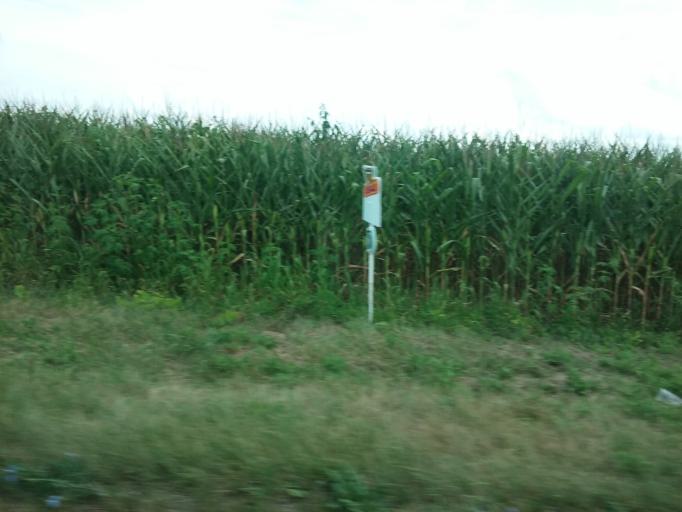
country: US
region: Ohio
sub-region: Hancock County
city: Findlay
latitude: 41.0422
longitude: -83.6887
